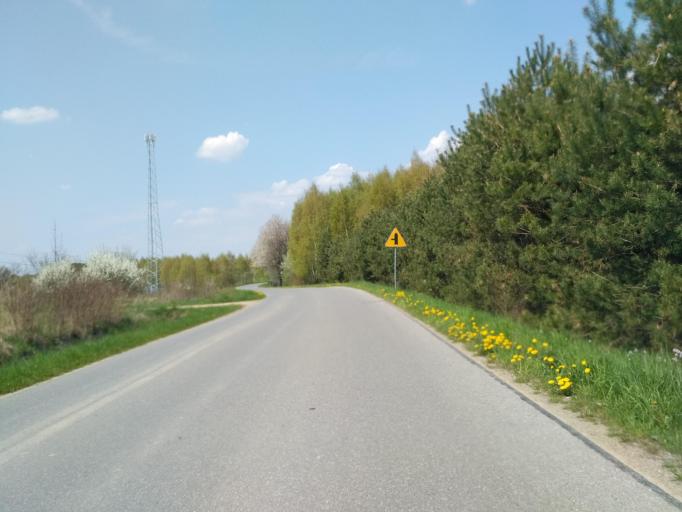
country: PL
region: Subcarpathian Voivodeship
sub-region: Powiat jasielski
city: Osiek Jasielski
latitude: 49.6786
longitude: 21.5142
